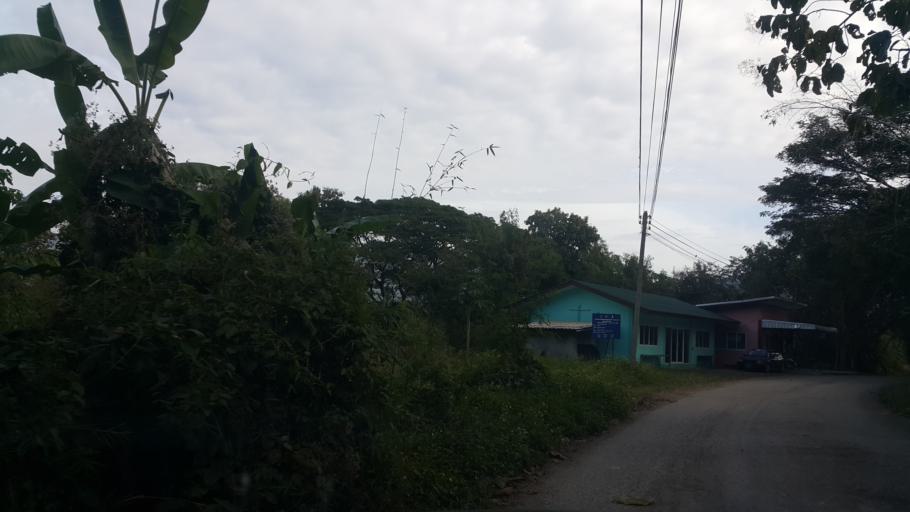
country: TH
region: Chiang Mai
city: Mae On
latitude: 18.7544
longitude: 99.2363
